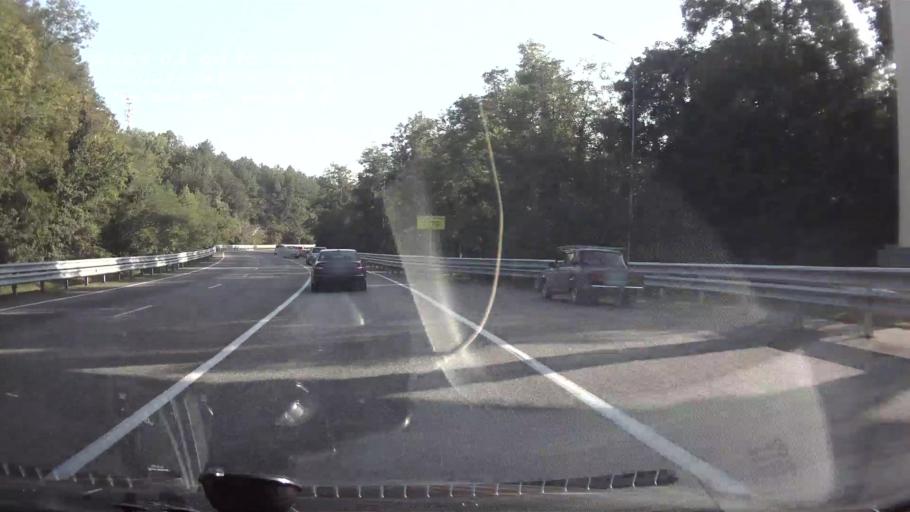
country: RU
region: Krasnodarskiy
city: Shepsi
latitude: 44.0271
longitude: 39.1581
